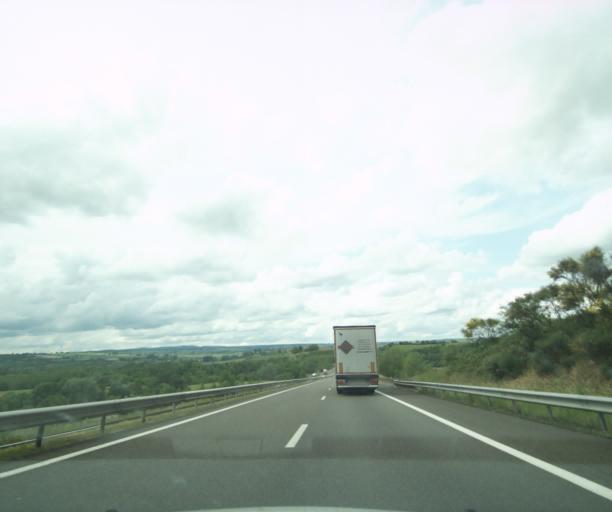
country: FR
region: Auvergne
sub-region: Departement de l'Allier
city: Ebreuil
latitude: 46.1195
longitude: 3.1231
